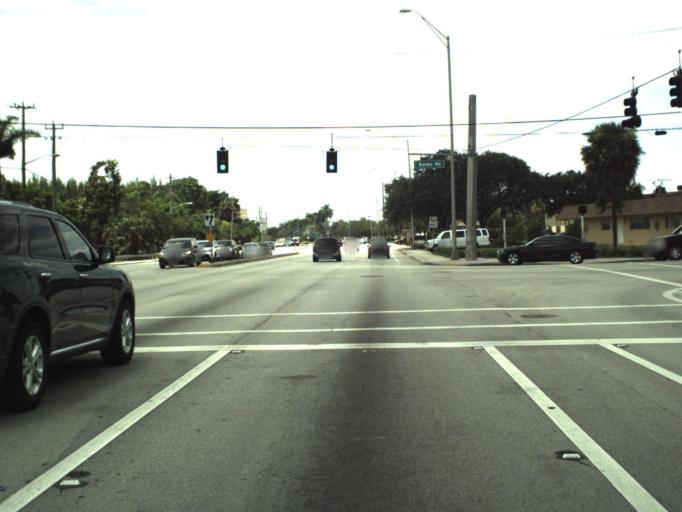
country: US
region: Florida
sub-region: Broward County
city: Margate
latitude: 26.2345
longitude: -80.1943
